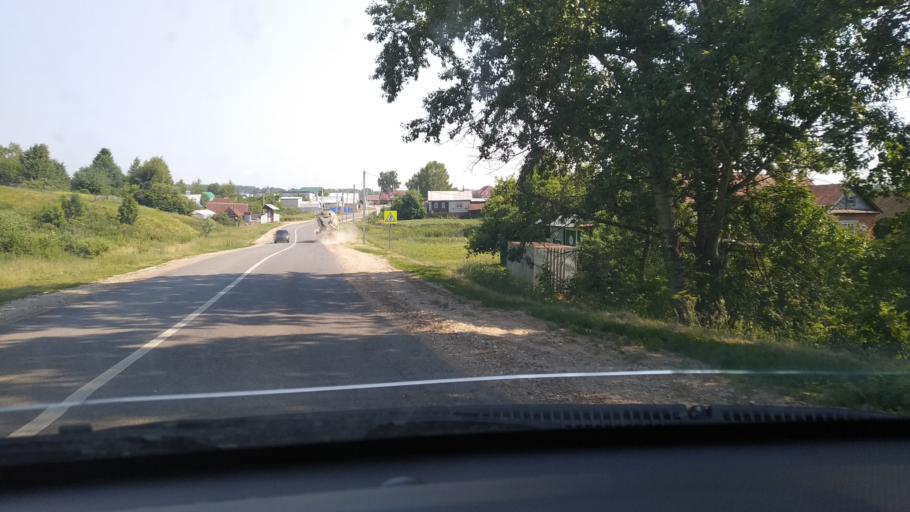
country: RU
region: Tatarstan
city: Osinovo
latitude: 55.9798
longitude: 48.7895
